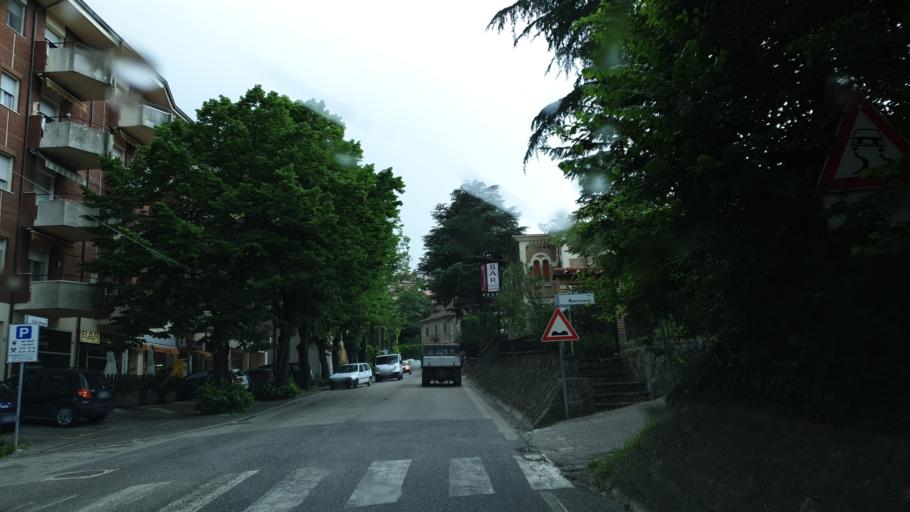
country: IT
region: Emilia-Romagna
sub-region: Provincia di Rimini
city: Novafeltria
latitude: 43.8968
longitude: 12.2883
